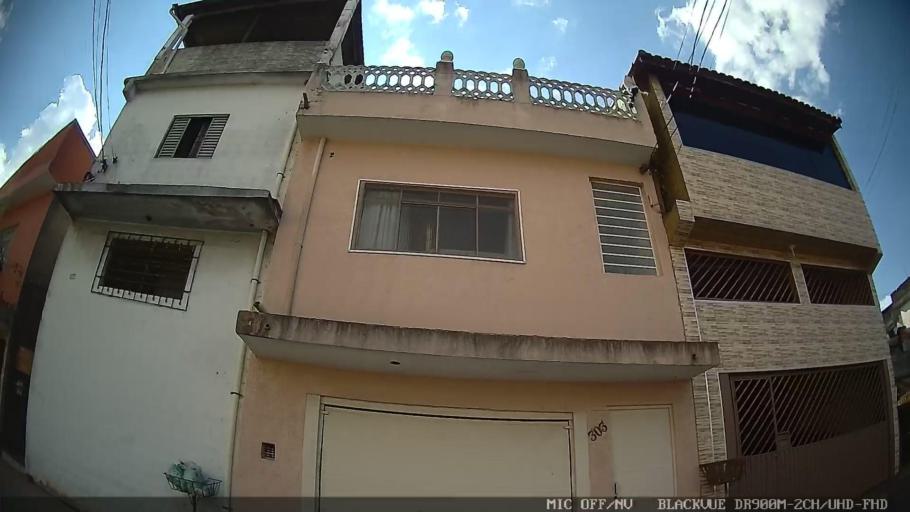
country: BR
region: Sao Paulo
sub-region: Ferraz De Vasconcelos
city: Ferraz de Vasconcelos
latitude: -23.5339
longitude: -46.4152
